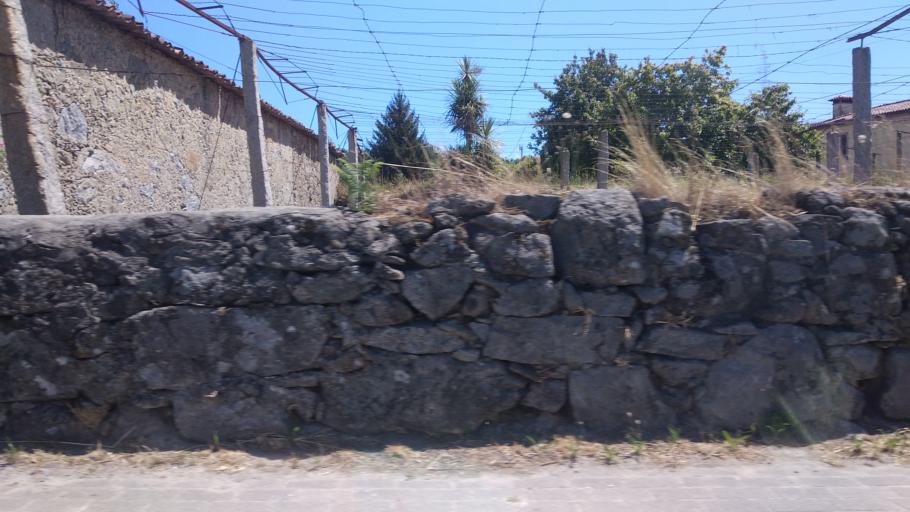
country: PT
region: Braga
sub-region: Vila Verde
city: Prado
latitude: 41.6035
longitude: -8.4675
